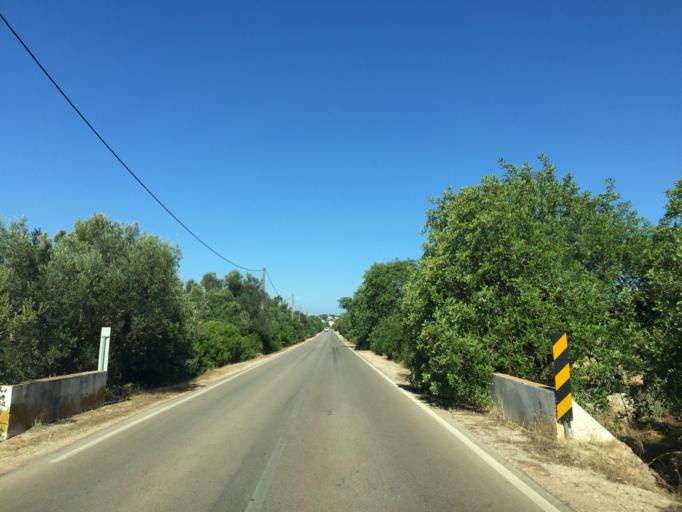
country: PT
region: Faro
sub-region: Loule
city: Almancil
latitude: 37.1102
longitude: -8.0695
